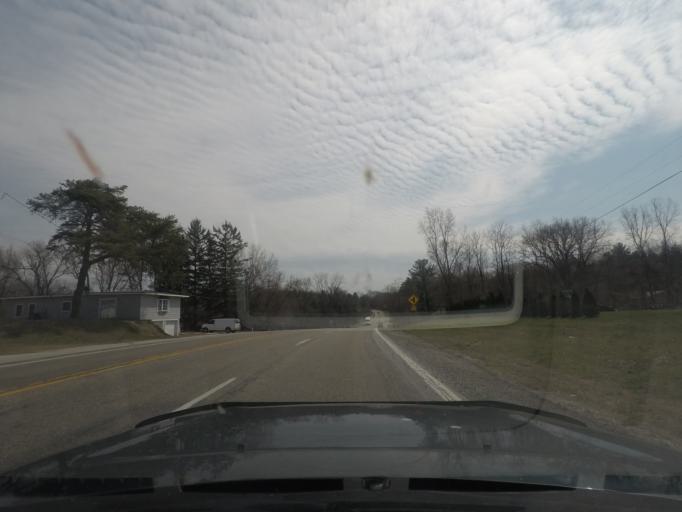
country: US
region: Indiana
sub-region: LaPorte County
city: LaPorte
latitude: 41.6650
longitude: -86.7732
